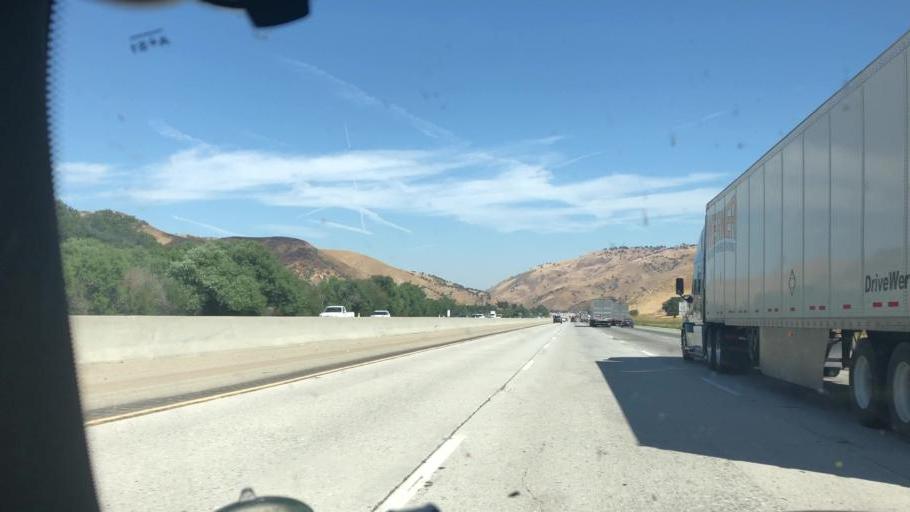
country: US
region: California
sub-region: Kern County
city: Lebec
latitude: 34.8471
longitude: -118.8683
